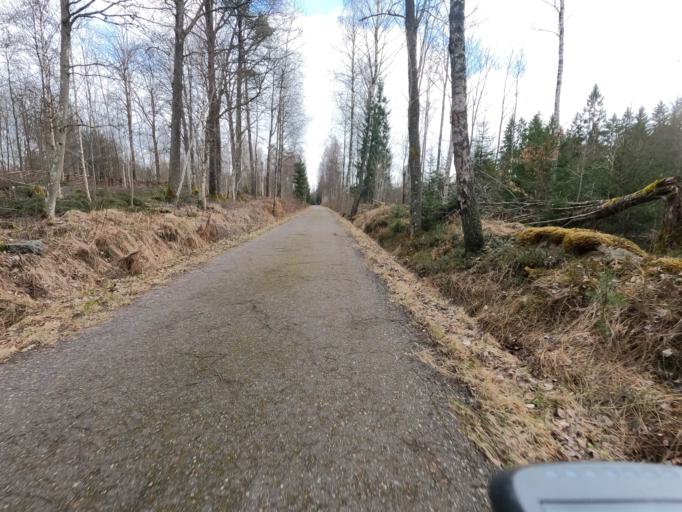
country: SE
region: Joenkoeping
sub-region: Varnamo Kommun
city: Rydaholm
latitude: 56.8546
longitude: 14.1868
